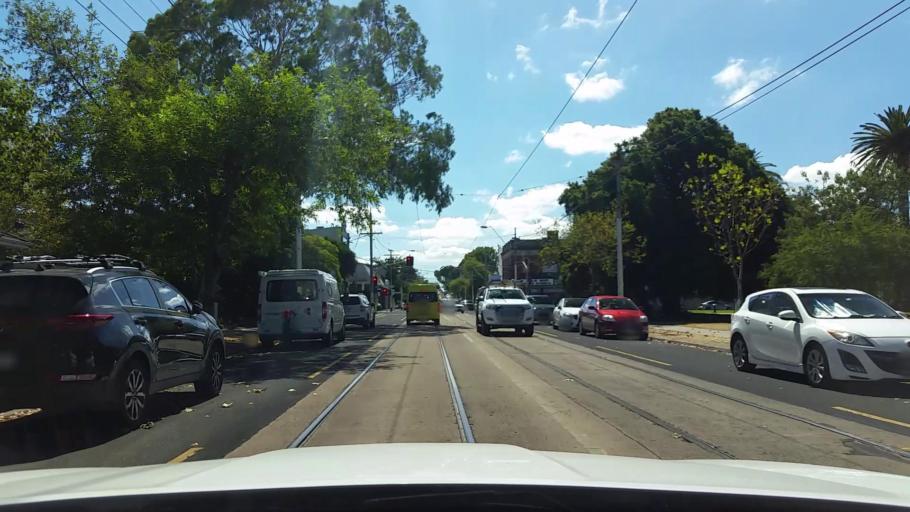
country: AU
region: Victoria
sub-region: Glen Eira
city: Caulfield North
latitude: -37.8705
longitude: 145.0251
